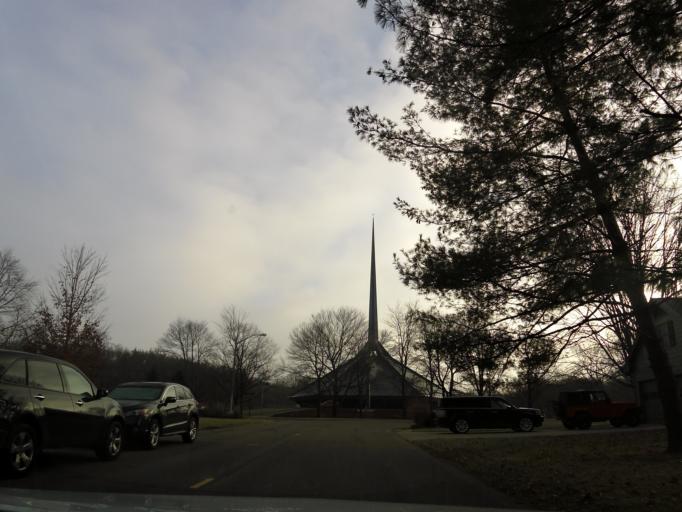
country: US
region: Indiana
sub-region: Bartholomew County
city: Columbus
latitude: 39.2298
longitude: -85.9178
